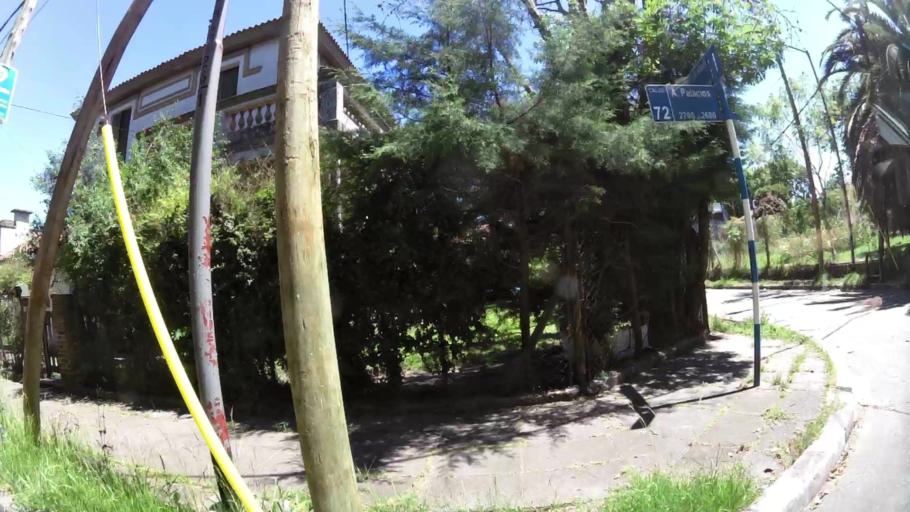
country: AR
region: Buenos Aires
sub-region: Partido de General San Martin
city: General San Martin
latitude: -34.5612
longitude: -58.5377
